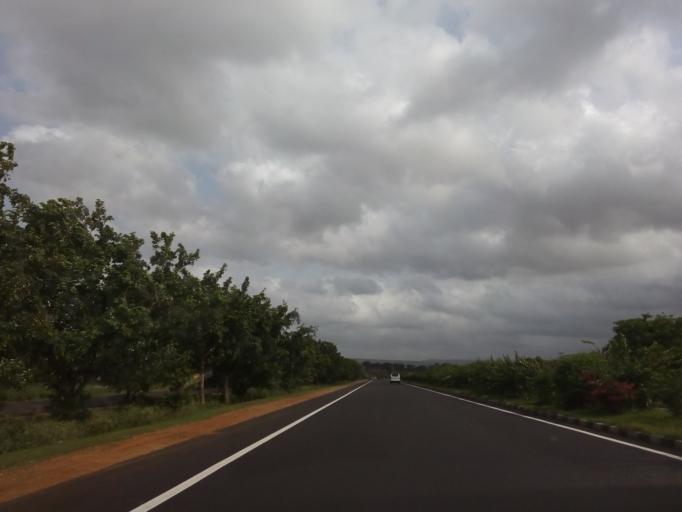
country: IN
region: Karnataka
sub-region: Belgaum
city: Hukeri
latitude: 16.1142
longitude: 74.5173
